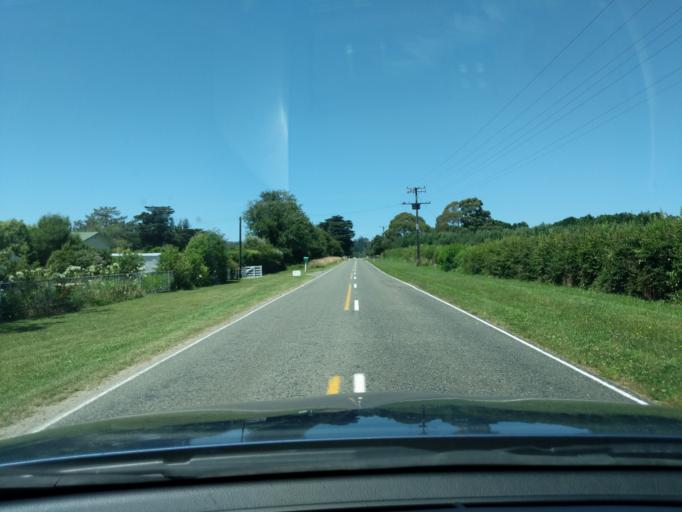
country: NZ
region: Tasman
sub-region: Tasman District
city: Takaka
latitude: -40.7297
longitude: 172.6193
